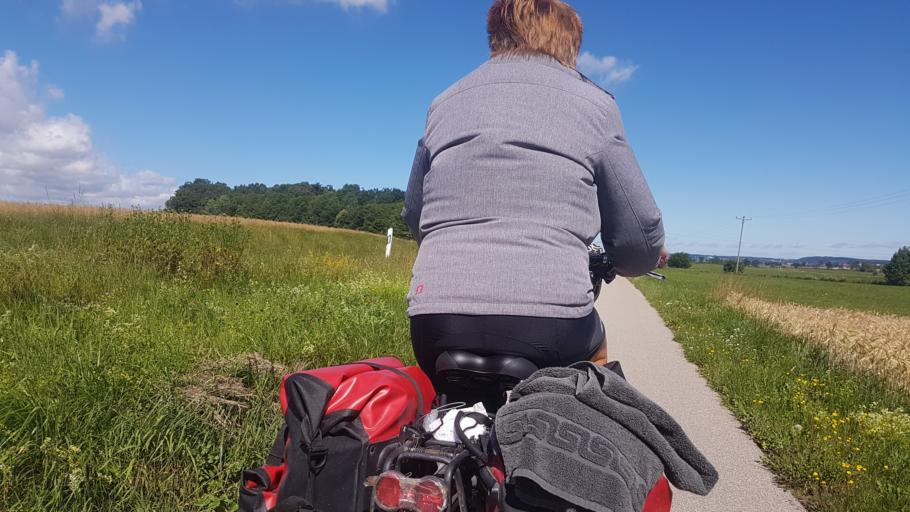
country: DE
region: Bavaria
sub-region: Regierungsbezirk Mittelfranken
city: Burgoberbach
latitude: 49.1953
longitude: 10.5661
